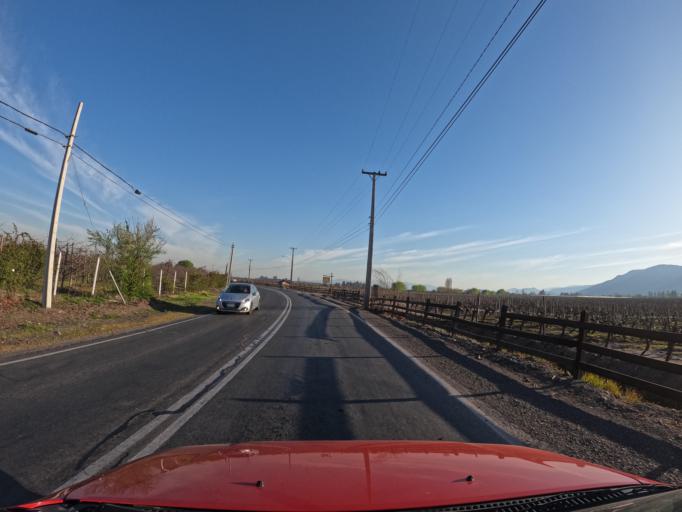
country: CL
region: Maule
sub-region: Provincia de Curico
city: Rauco
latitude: -34.9062
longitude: -71.2788
